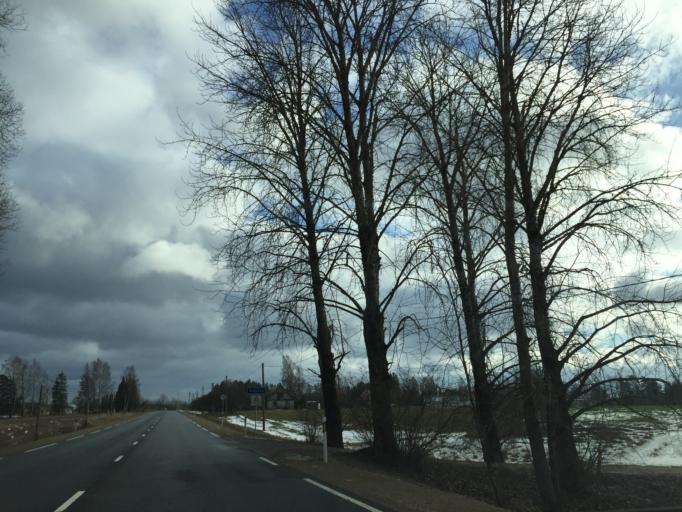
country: LV
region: Aloja
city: Staicele
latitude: 57.8413
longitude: 24.7369
